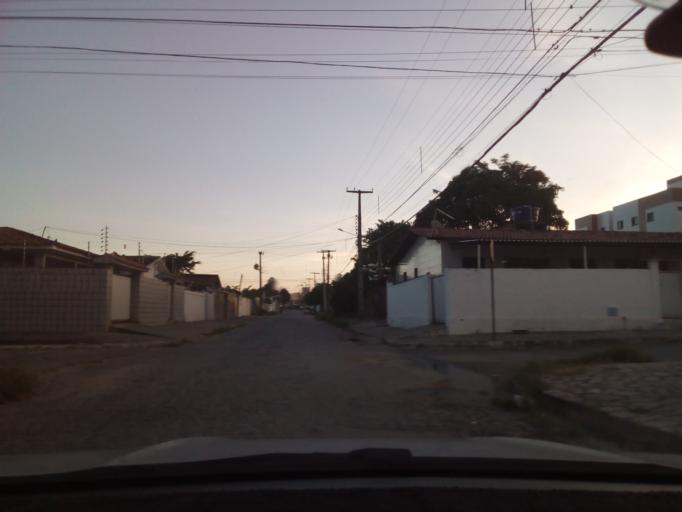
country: BR
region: Paraiba
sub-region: Joao Pessoa
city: Joao Pessoa
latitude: -7.1676
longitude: -34.8674
